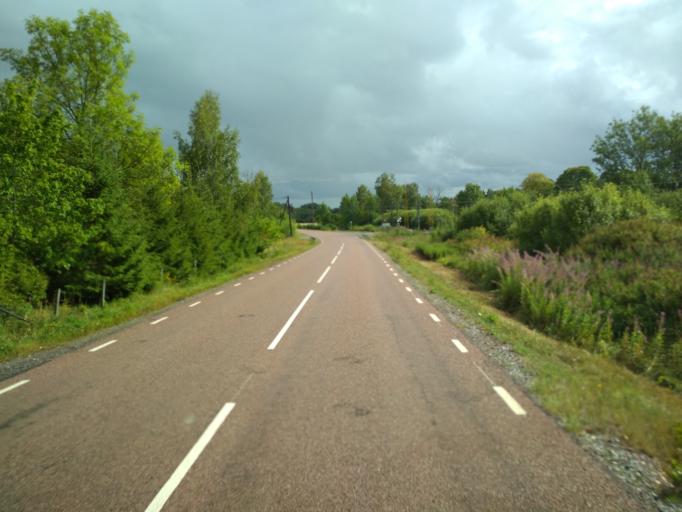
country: SE
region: Vaestmanland
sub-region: Surahammars Kommun
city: Ramnas
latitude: 59.8240
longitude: 16.1472
